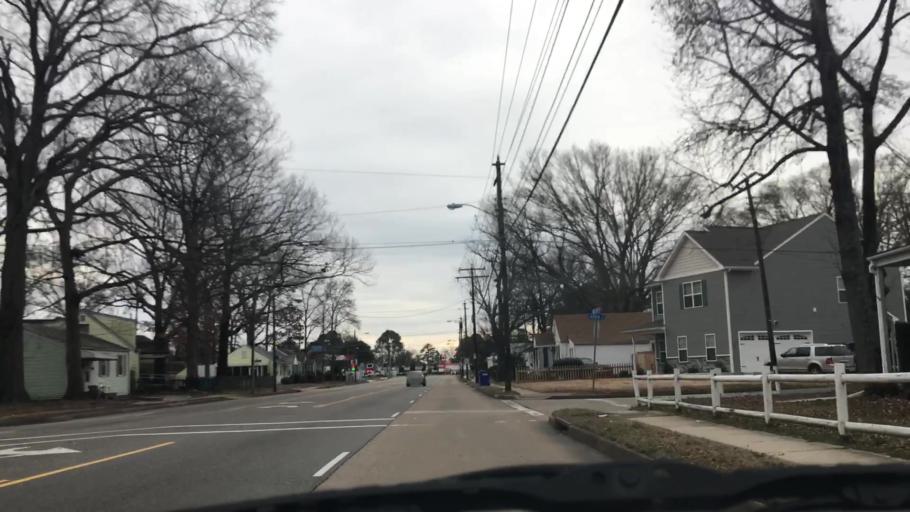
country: US
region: Virginia
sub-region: City of Norfolk
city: Norfolk
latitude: 36.8736
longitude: -76.2326
